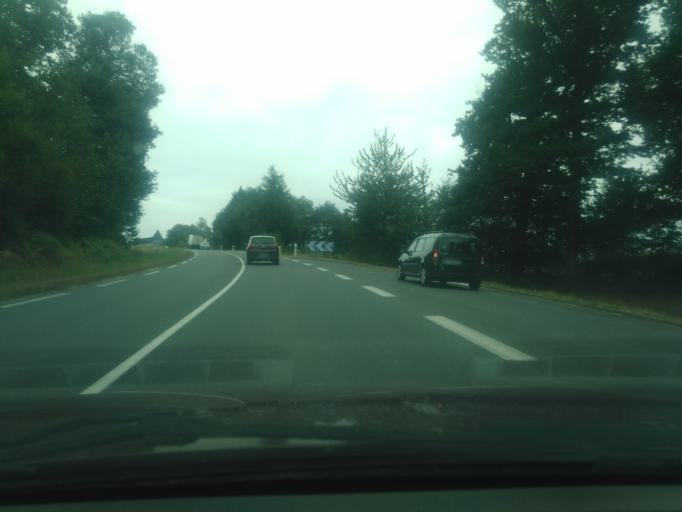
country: FR
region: Poitou-Charentes
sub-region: Departement de la Vienne
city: Chauvigny
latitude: 46.5714
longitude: 0.7284
